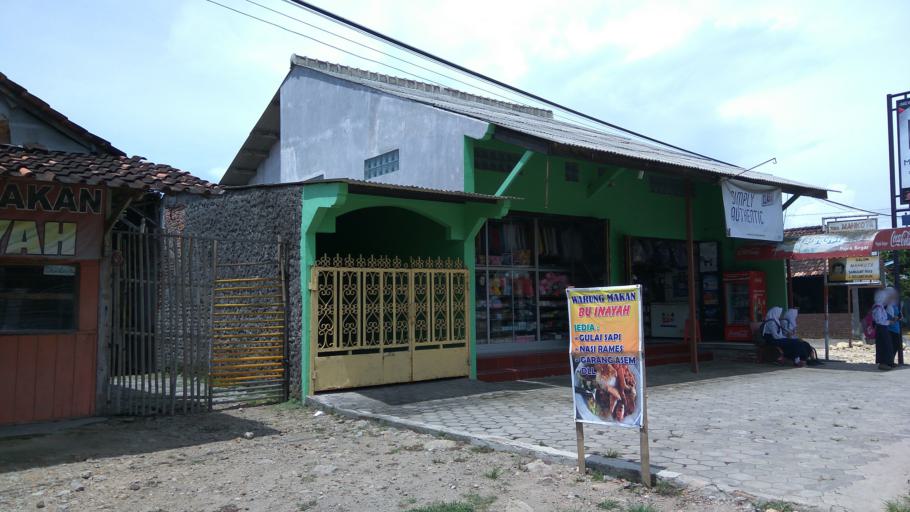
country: ID
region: Central Java
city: Mranggen
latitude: -7.0506
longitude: 110.6128
